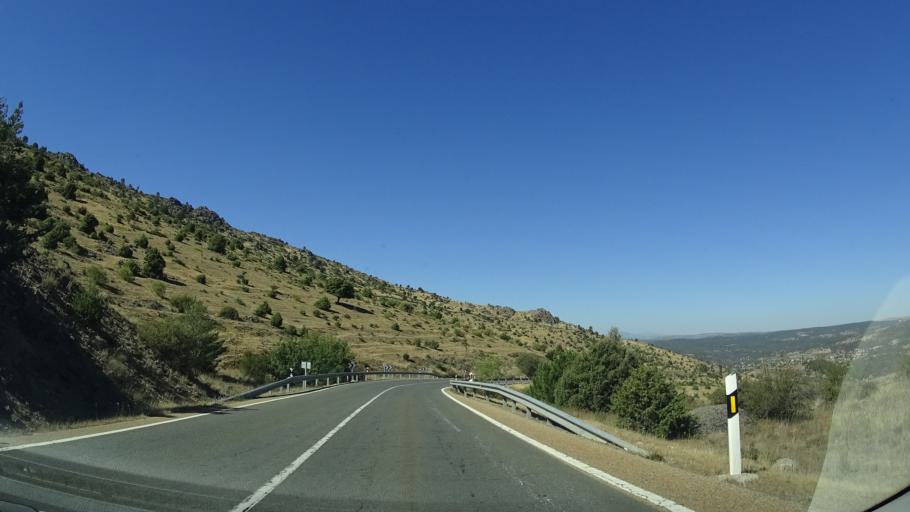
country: ES
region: Madrid
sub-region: Provincia de Madrid
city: Zarzalejo
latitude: 40.5610
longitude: -4.2224
